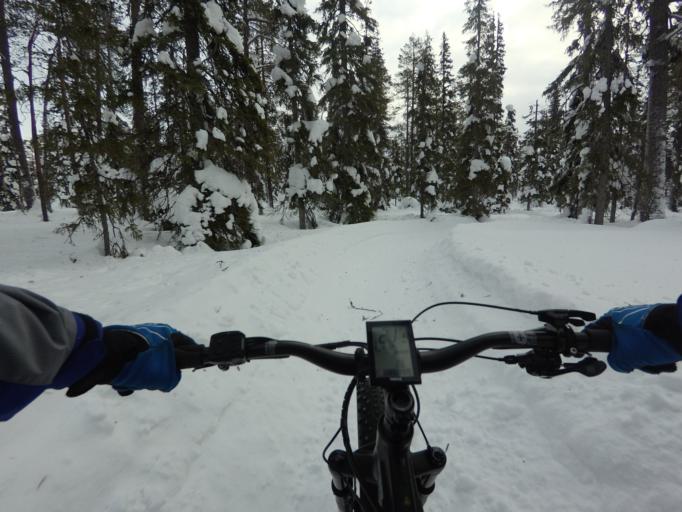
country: FI
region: Lapland
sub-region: Tunturi-Lappi
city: Kolari
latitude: 67.5990
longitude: 24.2860
